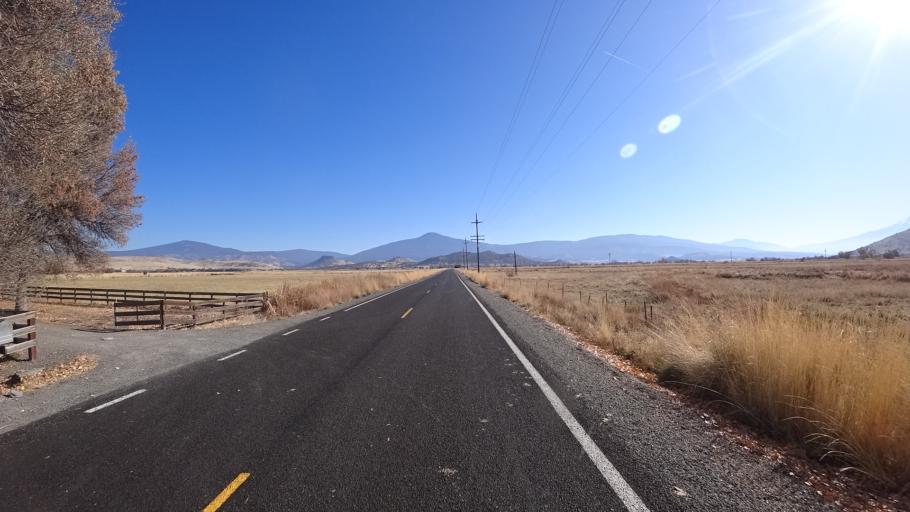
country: US
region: California
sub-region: Siskiyou County
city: Montague
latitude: 41.7113
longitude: -122.4113
